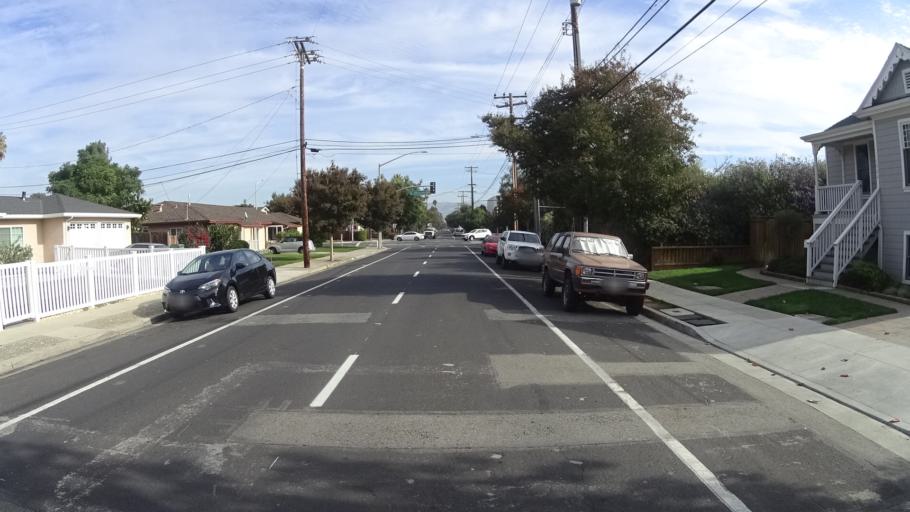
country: US
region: California
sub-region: Santa Clara County
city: Santa Clara
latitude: 37.3424
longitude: -121.9527
